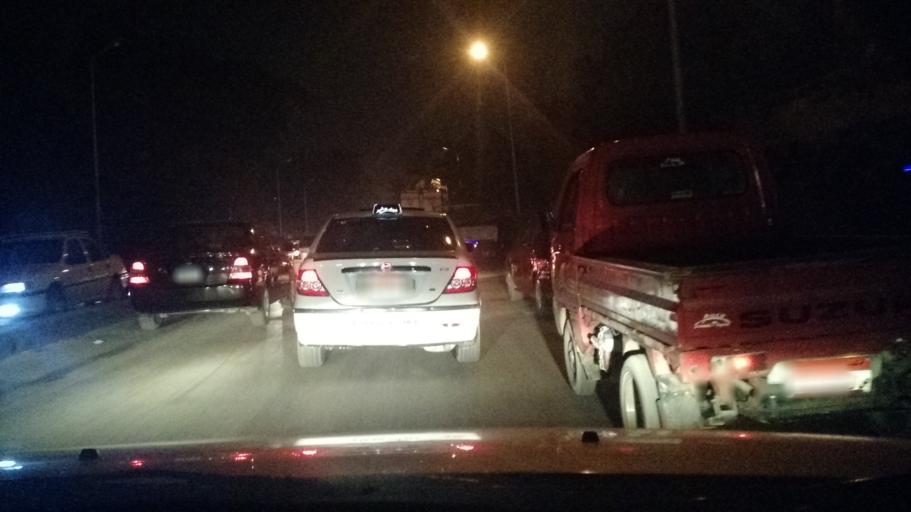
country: EG
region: Al Jizah
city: Al Jizah
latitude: 30.0197
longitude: 31.2470
